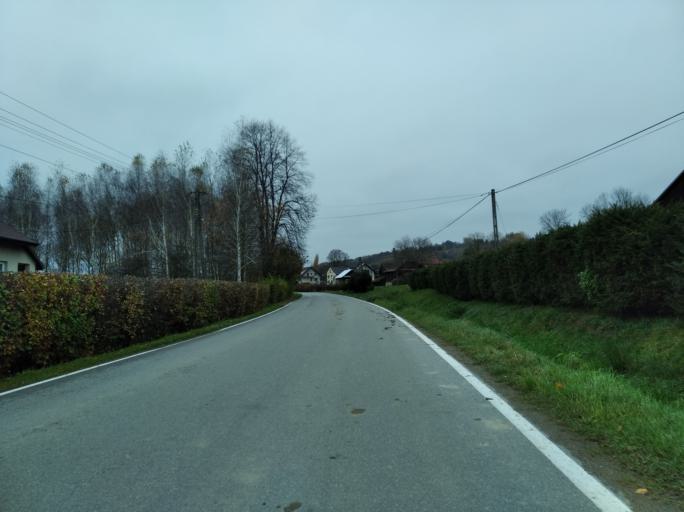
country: PL
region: Subcarpathian Voivodeship
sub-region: Powiat krosnienski
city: Leki
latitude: 49.8161
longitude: 21.6520
